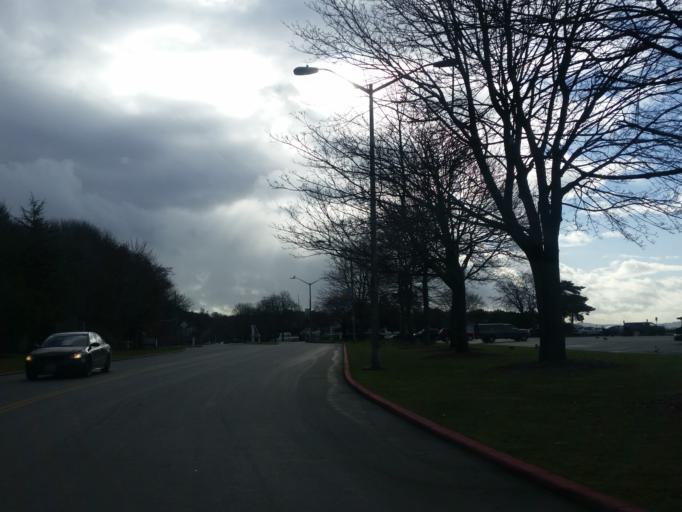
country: US
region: Washington
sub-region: King County
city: Shoreline
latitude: 47.6891
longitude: -122.4025
